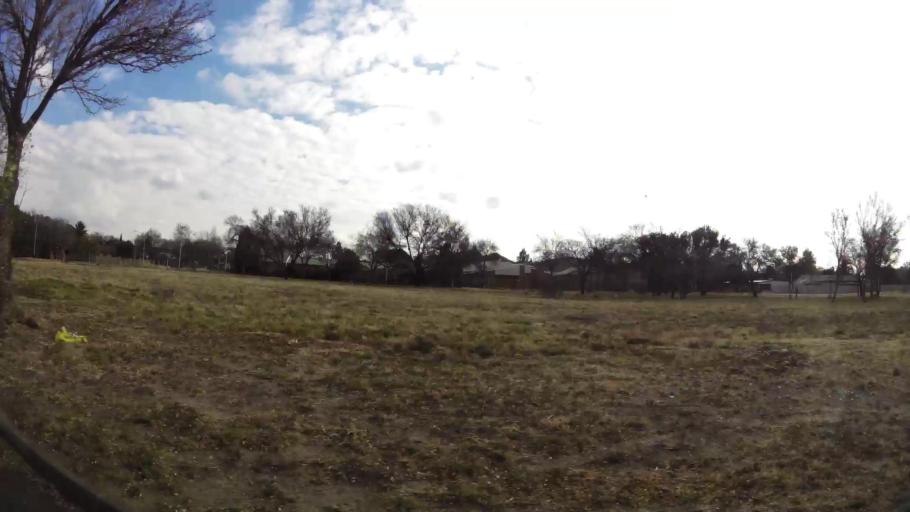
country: ZA
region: Orange Free State
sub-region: Mangaung Metropolitan Municipality
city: Bloemfontein
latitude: -29.0841
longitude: 26.2395
